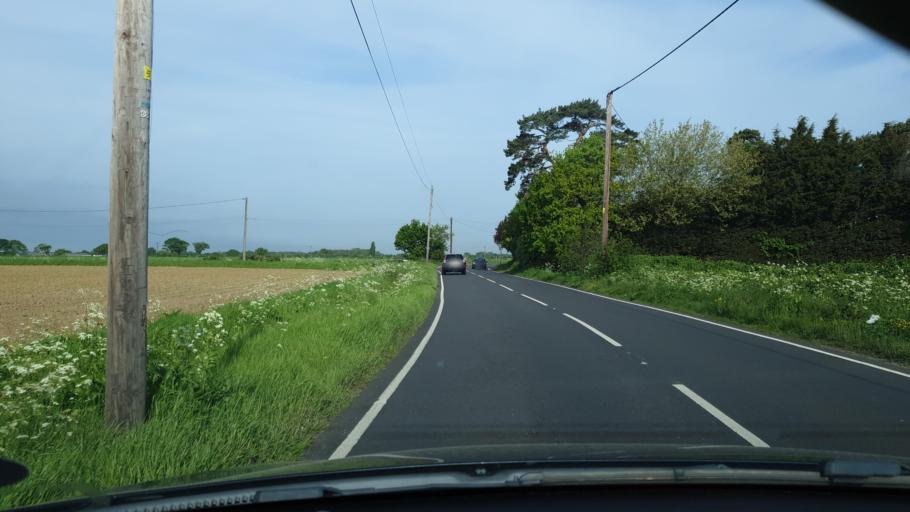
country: GB
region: England
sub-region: Essex
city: Frinton-on-Sea
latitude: 51.8465
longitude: 1.1962
